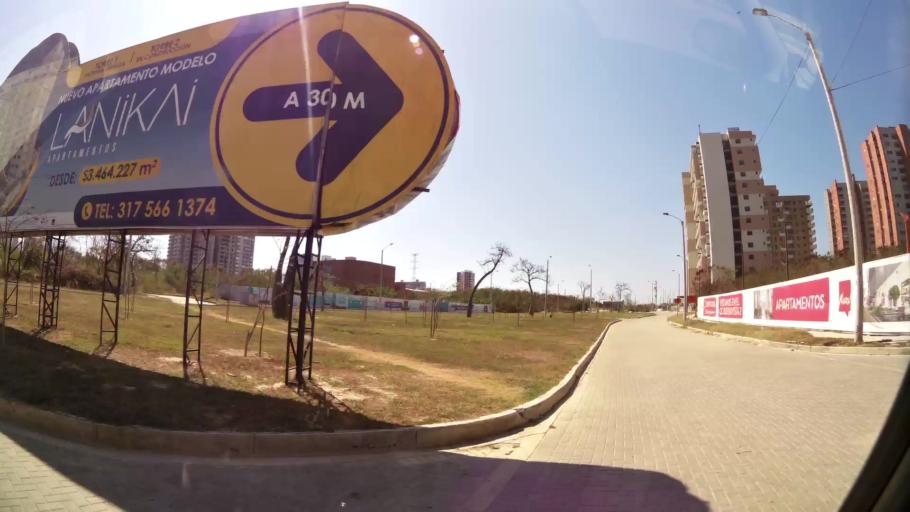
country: CO
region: Atlantico
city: Barranquilla
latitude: 11.0193
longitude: -74.8393
